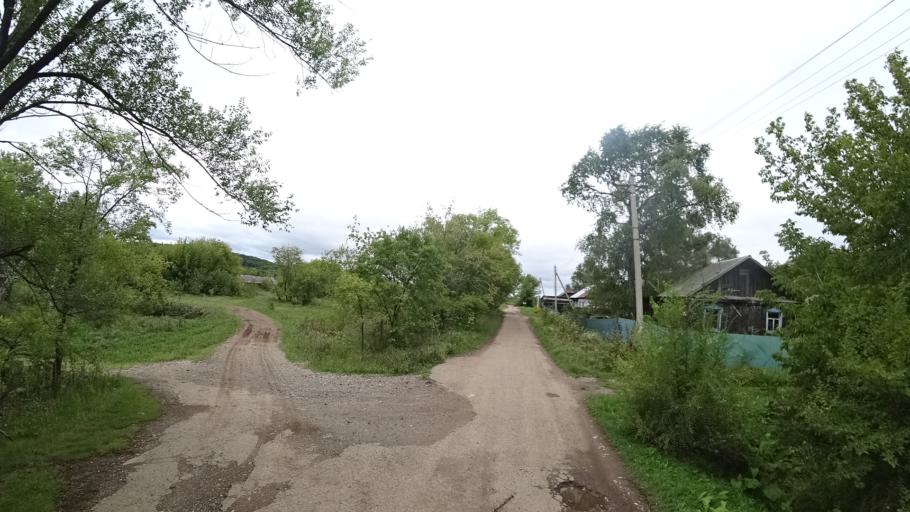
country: RU
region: Primorskiy
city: Chernigovka
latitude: 44.4605
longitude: 132.5903
